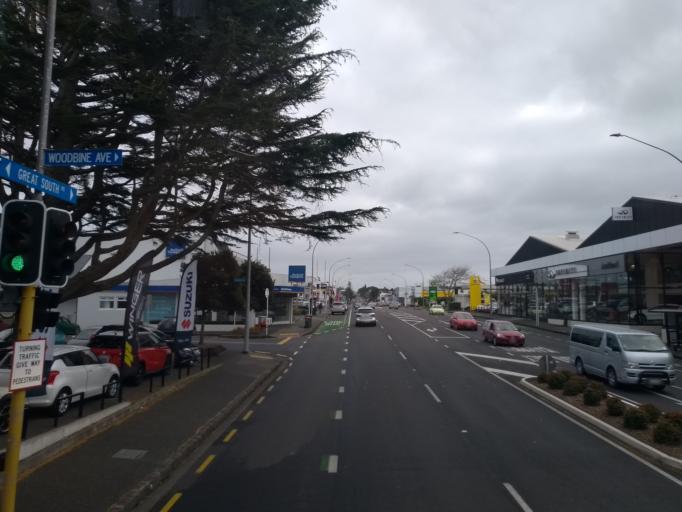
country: NZ
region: Auckland
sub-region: Auckland
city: Auckland
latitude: -36.8934
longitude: 174.7980
